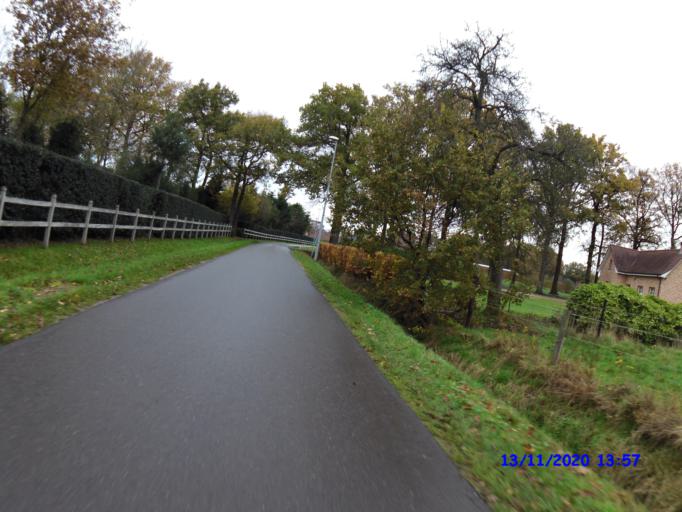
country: BE
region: Flanders
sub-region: Provincie Antwerpen
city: Turnhout
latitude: 51.2926
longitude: 4.9585
